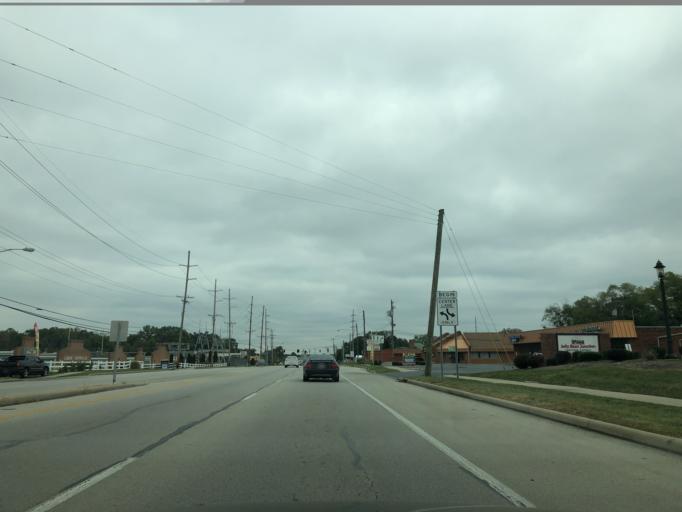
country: US
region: Ohio
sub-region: Warren County
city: Landen
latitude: 39.3043
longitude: -84.2820
